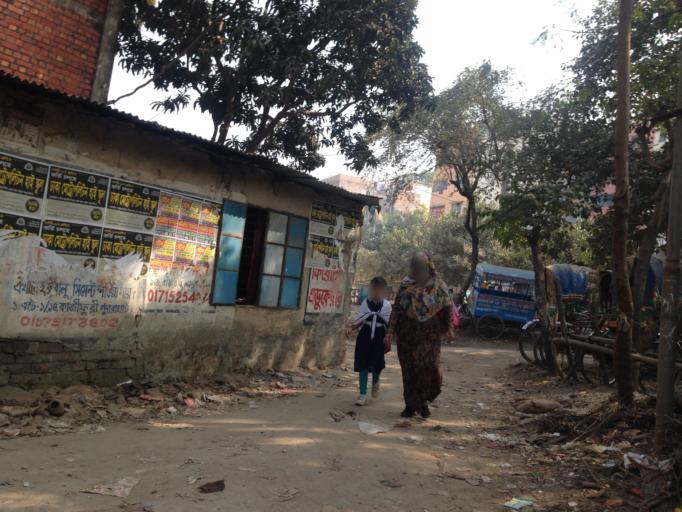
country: BD
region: Dhaka
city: Azimpur
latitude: 23.8053
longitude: 90.3480
